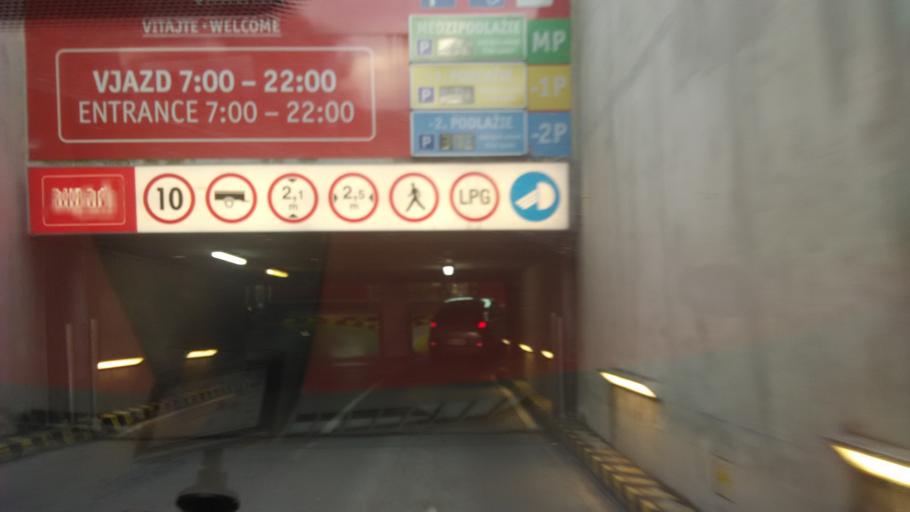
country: SK
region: Zilinsky
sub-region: Okres Zilina
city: Zilina
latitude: 49.2206
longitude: 18.7414
